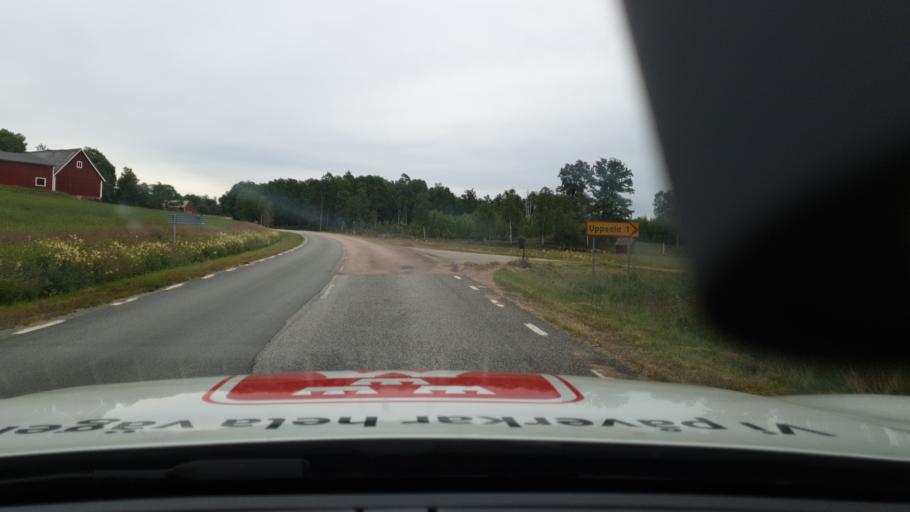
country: SE
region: Joenkoeping
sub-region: Varnamo Kommun
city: Forsheda
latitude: 57.0625
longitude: 13.9108
